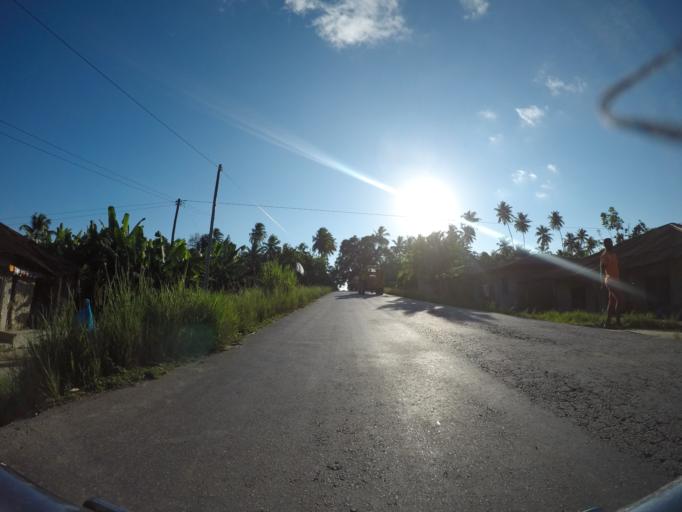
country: TZ
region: Pemba South
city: Mtambile
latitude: -5.3686
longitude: 39.7098
